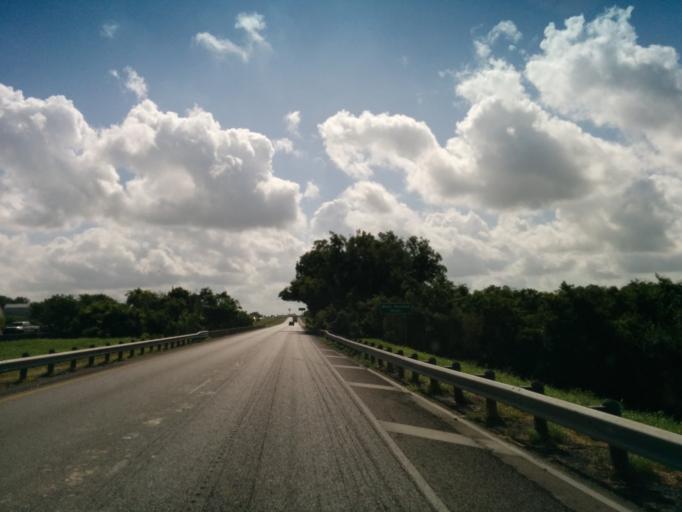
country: US
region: Texas
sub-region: Fayette County
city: Schulenburg
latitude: 29.6895
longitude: -96.9395
